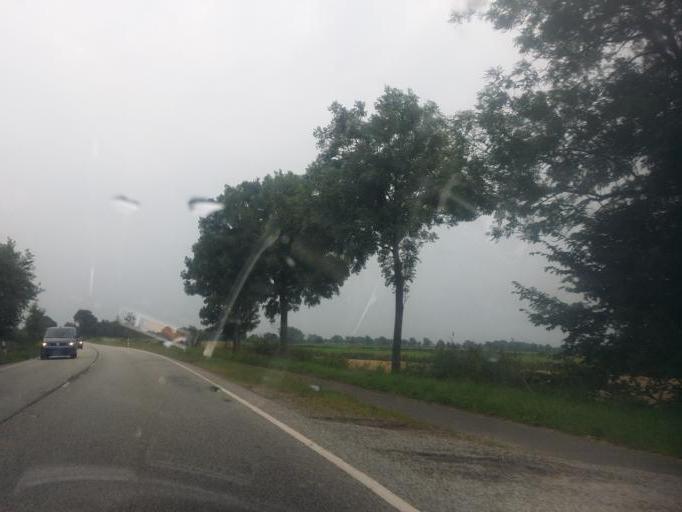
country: DE
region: Schleswig-Holstein
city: Husum
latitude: 54.4357
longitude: 9.0452
